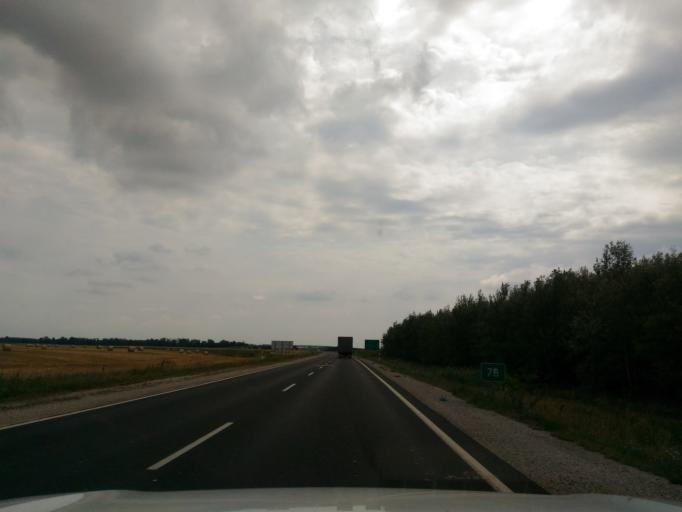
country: HU
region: Pest
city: Tortel
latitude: 47.1921
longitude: 19.9233
